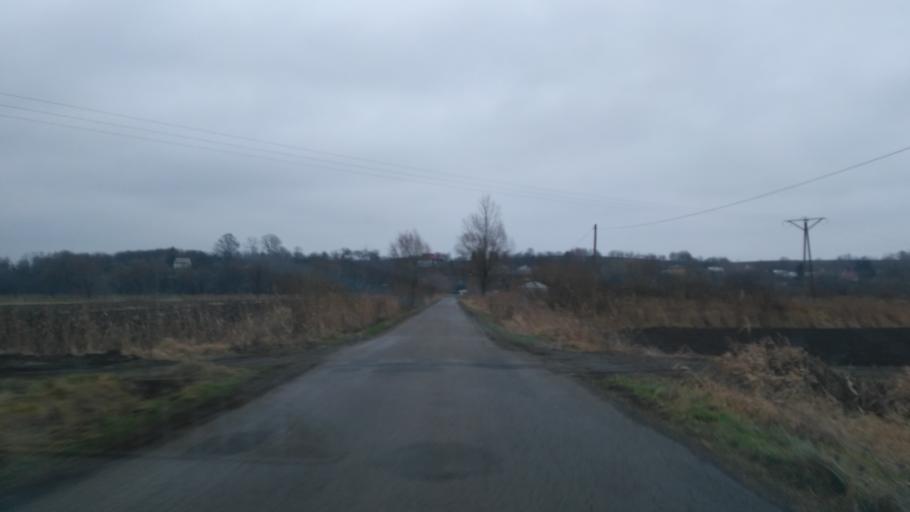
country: PL
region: Subcarpathian Voivodeship
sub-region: Powiat przeworski
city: Zarzecze
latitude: 49.9375
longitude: 22.5623
